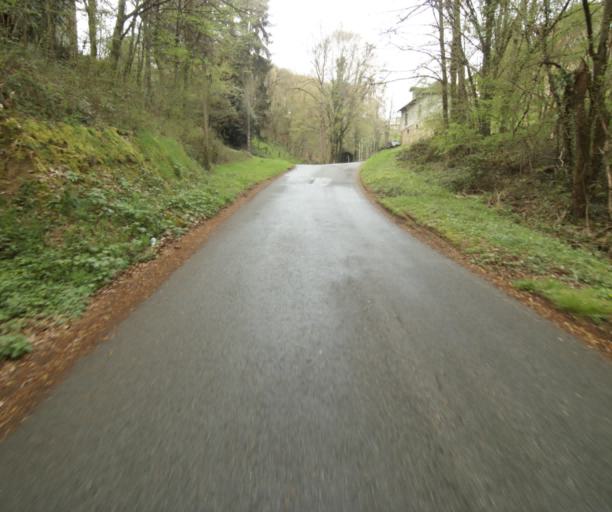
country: FR
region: Limousin
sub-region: Departement de la Correze
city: Tulle
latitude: 45.2630
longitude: 1.7524
